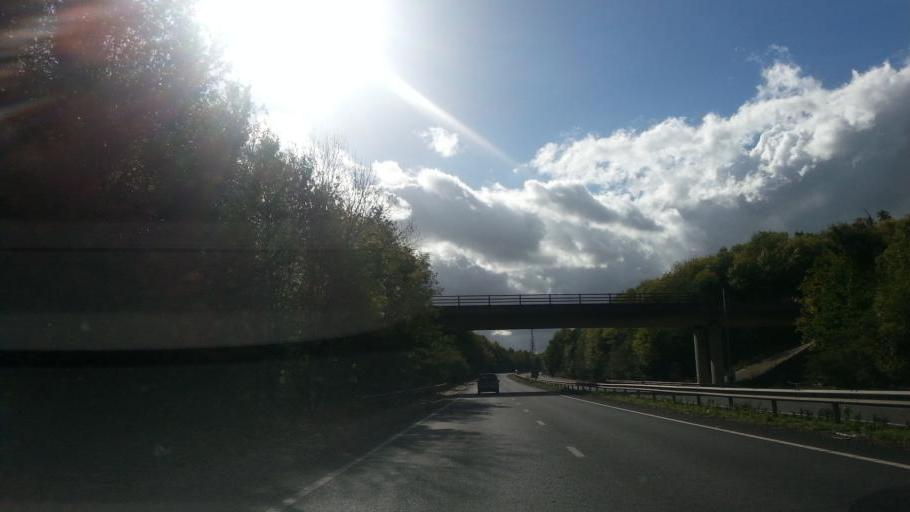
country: GB
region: England
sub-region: Cambridgeshire
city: Girton
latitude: 52.2221
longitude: 0.0491
